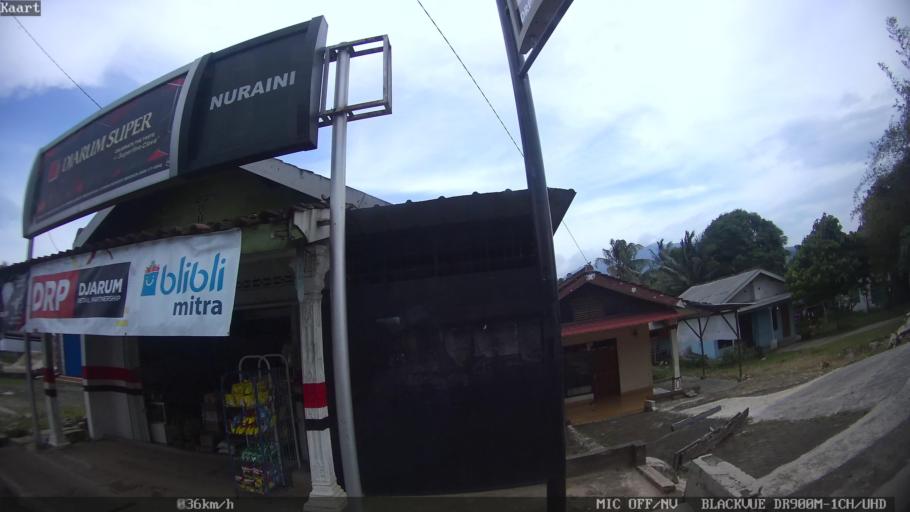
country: ID
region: Lampung
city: Kedaton
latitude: -5.3882
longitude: 105.2047
